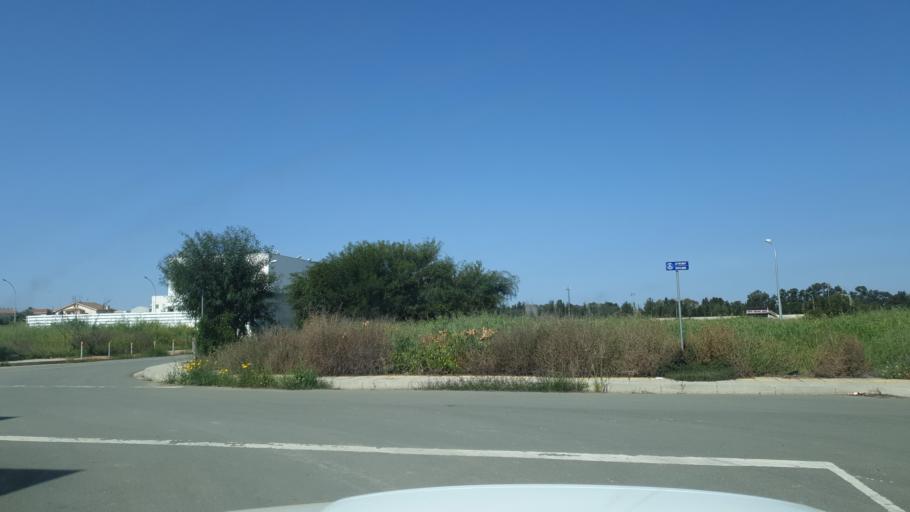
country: CY
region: Lefkosia
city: Tseri
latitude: 35.1308
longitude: 33.3211
